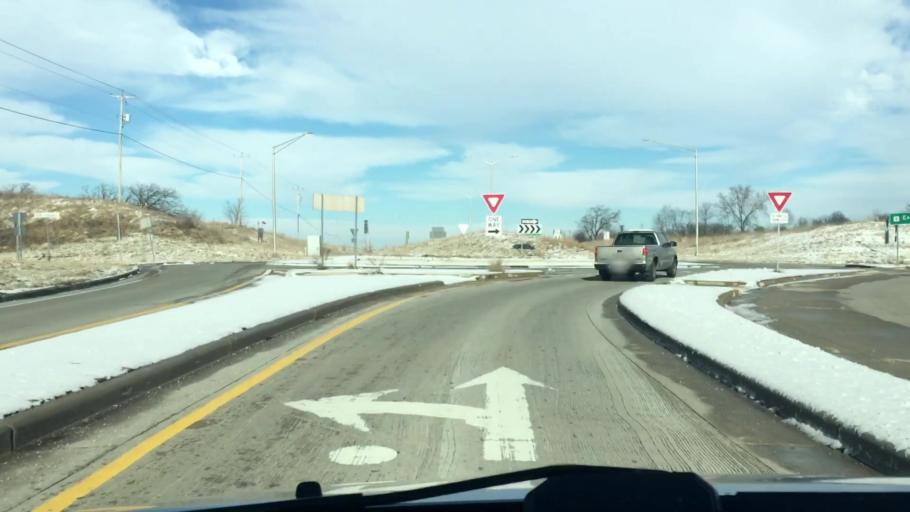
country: US
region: Wisconsin
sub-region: Waukesha County
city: North Prairie
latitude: 42.9341
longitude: -88.3464
